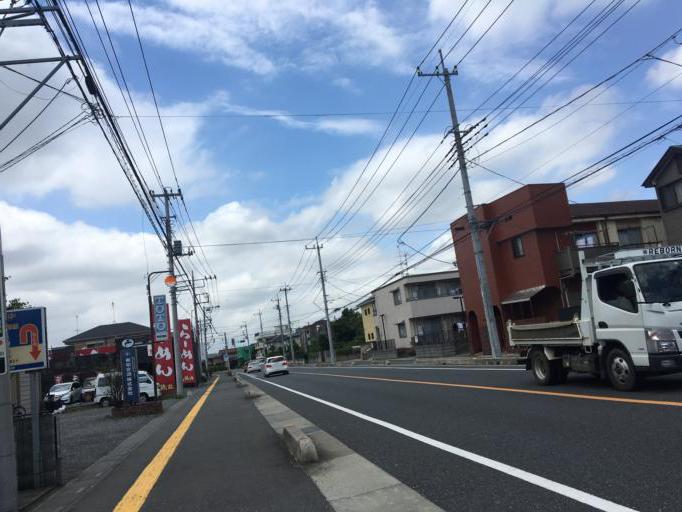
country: JP
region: Saitama
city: Okegawa
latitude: 35.9926
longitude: 139.5741
